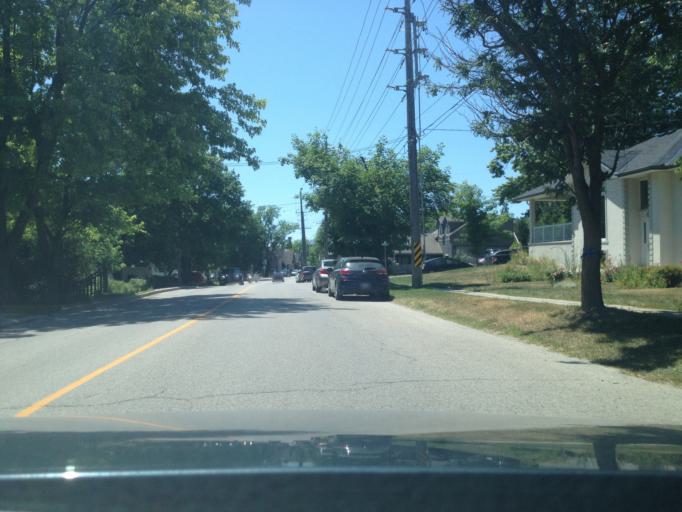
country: CA
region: Ontario
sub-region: Wellington County
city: Guelph
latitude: 43.6827
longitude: -80.4268
